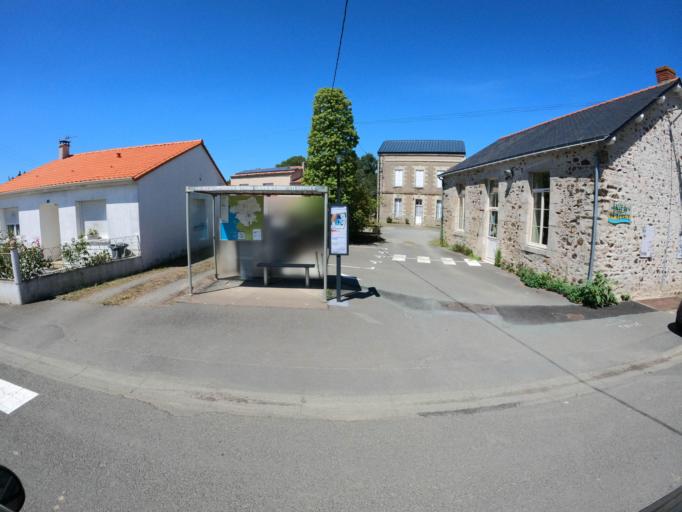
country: FR
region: Pays de la Loire
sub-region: Departement de la Loire-Atlantique
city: La Limouziniere
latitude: 46.9549
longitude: -1.6052
